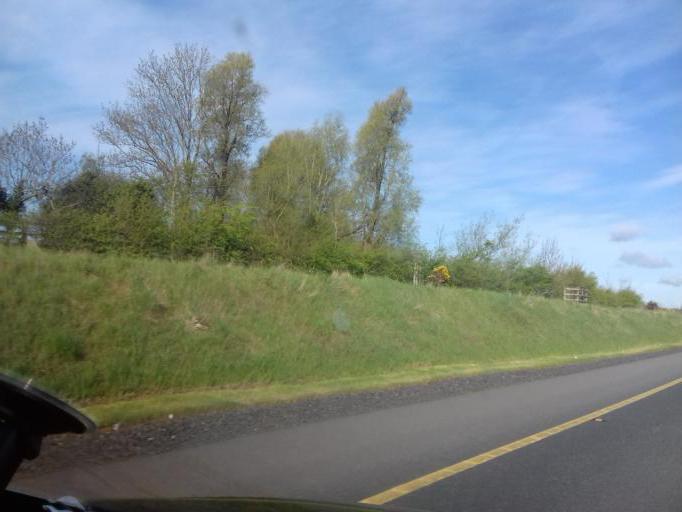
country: IE
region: Leinster
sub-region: An Mhi
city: Kells
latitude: 53.6952
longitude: -6.8290
